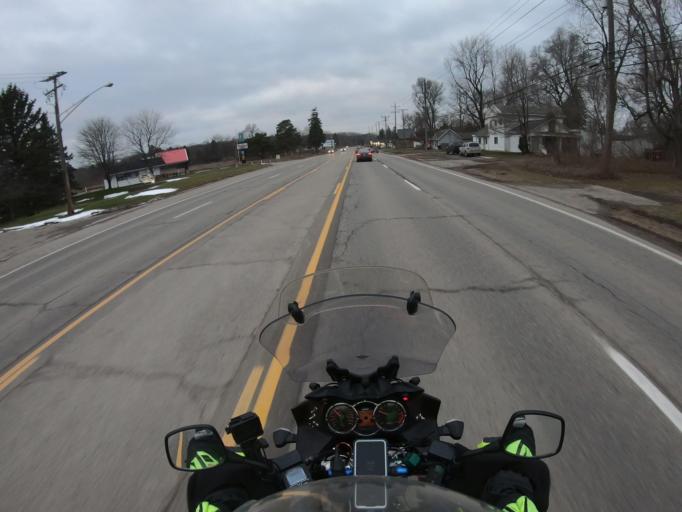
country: US
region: Michigan
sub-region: Oakland County
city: Clarkston
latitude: 42.7487
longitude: -83.4718
